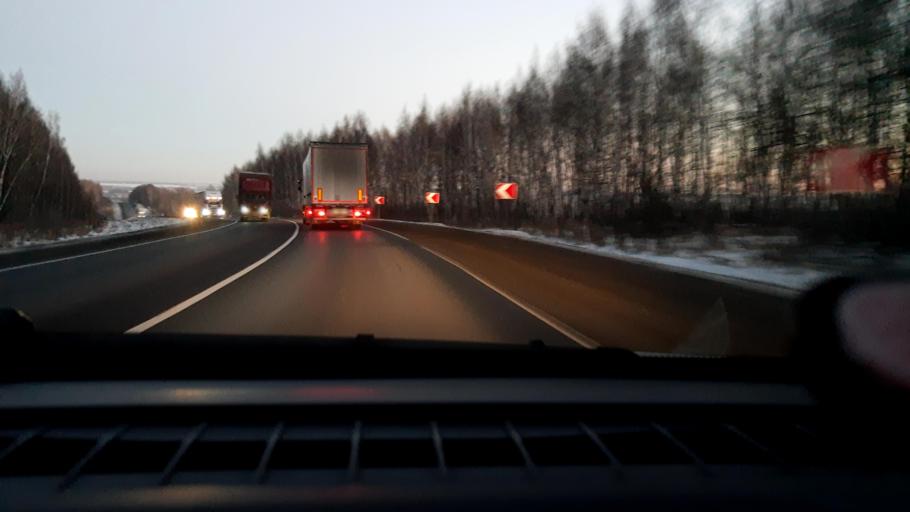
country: RU
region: Nizjnij Novgorod
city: Lyskovo
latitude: 56.0091
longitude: 44.8693
